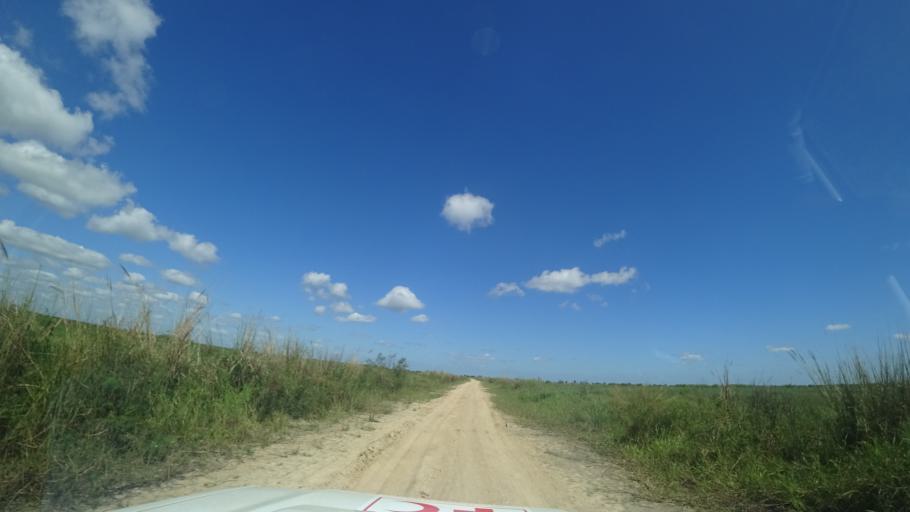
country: MZ
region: Sofala
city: Dondo
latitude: -19.3922
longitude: 34.5758
